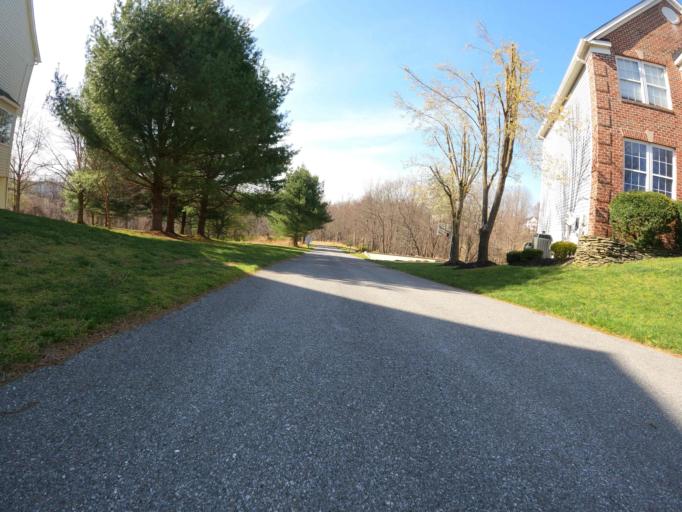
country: US
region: Maryland
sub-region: Howard County
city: Ellicott City
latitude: 39.3065
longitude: -76.8125
